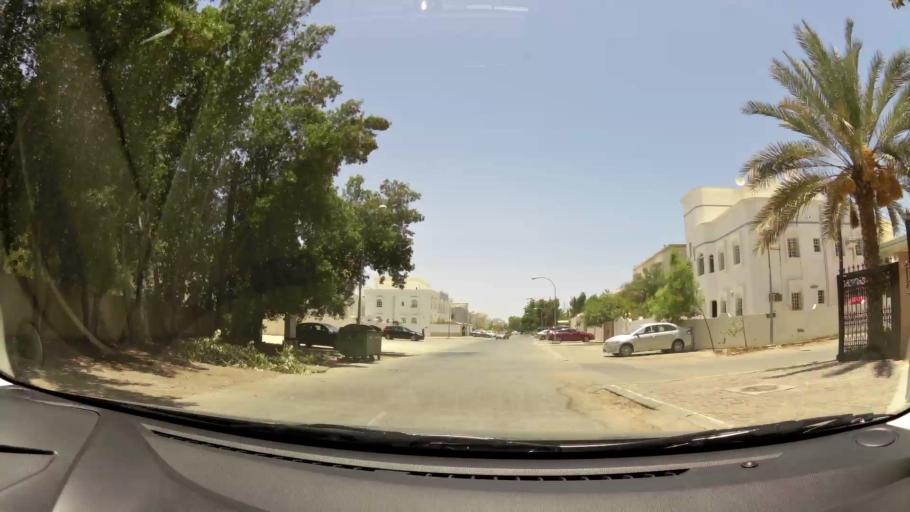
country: OM
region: Muhafazat Masqat
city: Bawshar
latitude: 23.5973
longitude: 58.3952
